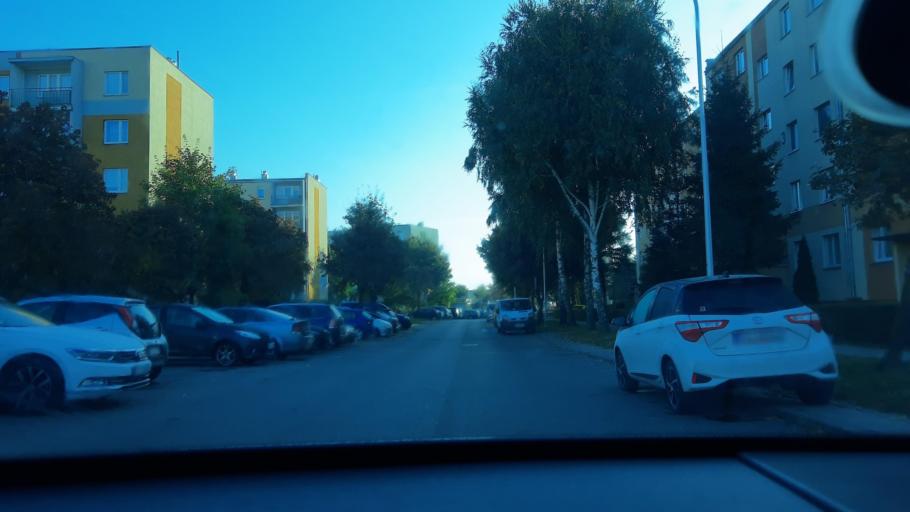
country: PL
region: Lodz Voivodeship
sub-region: Powiat sieradzki
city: Sieradz
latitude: 51.5925
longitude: 18.7117
